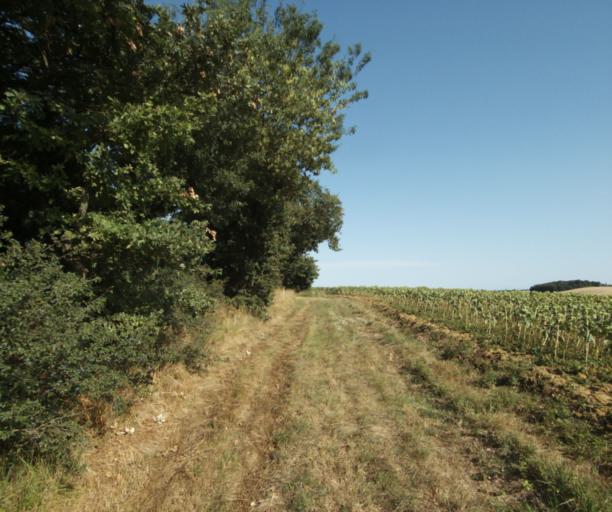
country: FR
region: Midi-Pyrenees
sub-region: Departement de la Haute-Garonne
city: Avignonet-Lauragais
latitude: 43.4258
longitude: 1.8036
